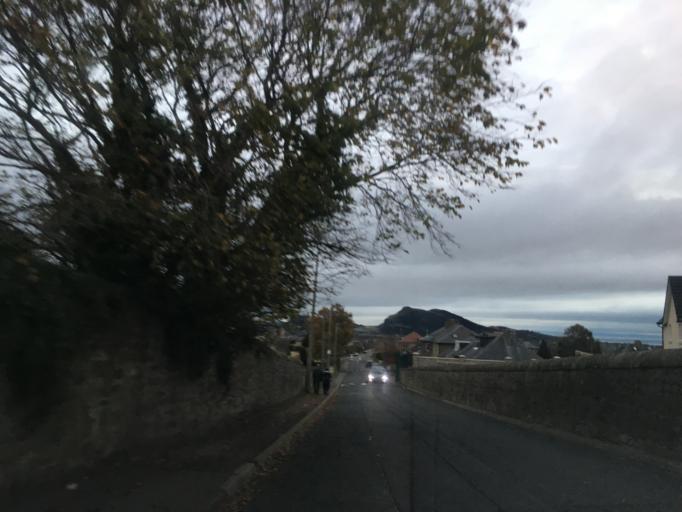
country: GB
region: Scotland
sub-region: Midlothian
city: Loanhead
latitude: 55.9097
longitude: -3.1686
